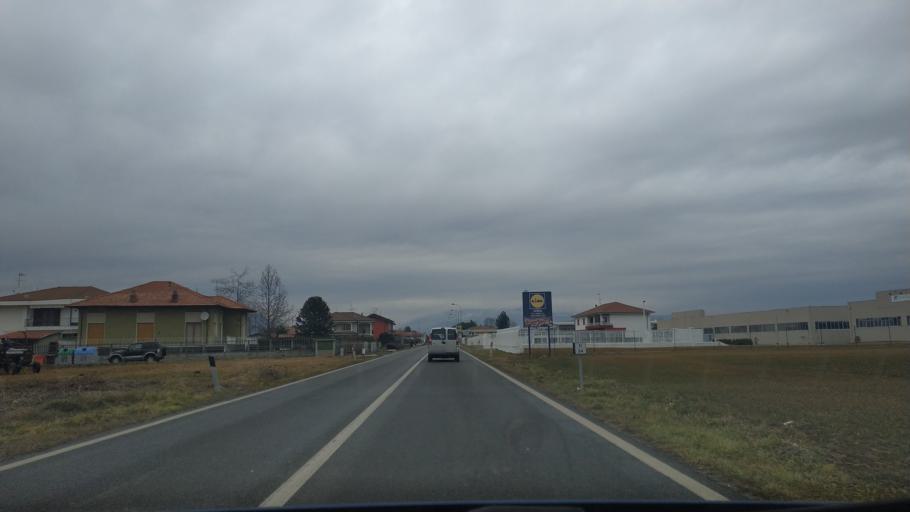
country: IT
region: Piedmont
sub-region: Provincia di Torino
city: Strambino
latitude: 45.3924
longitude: 7.8846
